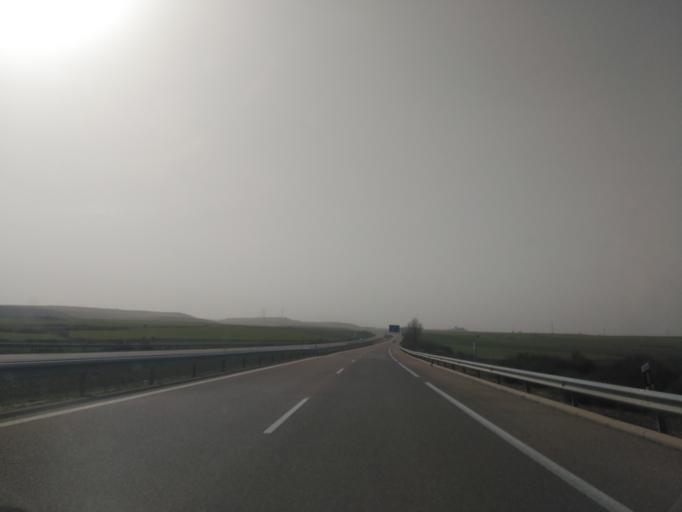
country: ES
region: Castille and Leon
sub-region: Provincia de Palencia
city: Monzon de Campos
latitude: 42.1341
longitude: -4.4727
